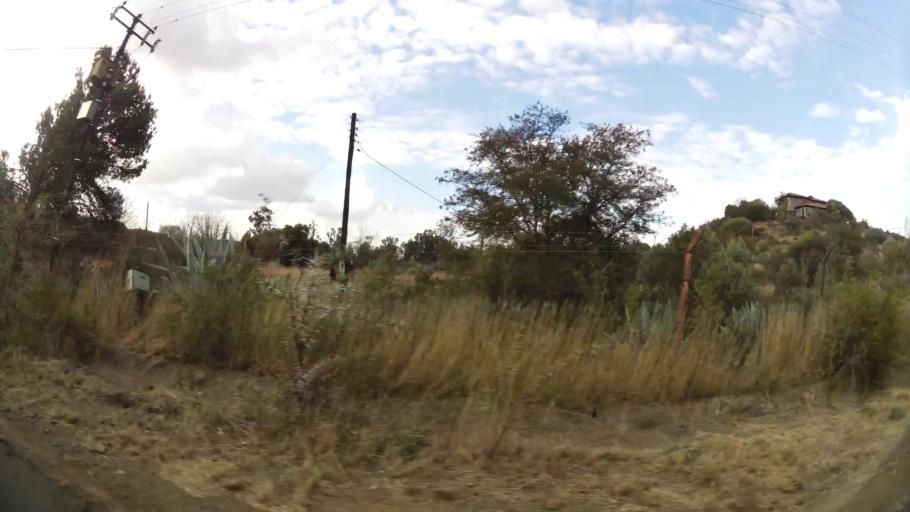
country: ZA
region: Orange Free State
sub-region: Mangaung Metropolitan Municipality
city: Bloemfontein
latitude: -29.0734
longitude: 26.2063
